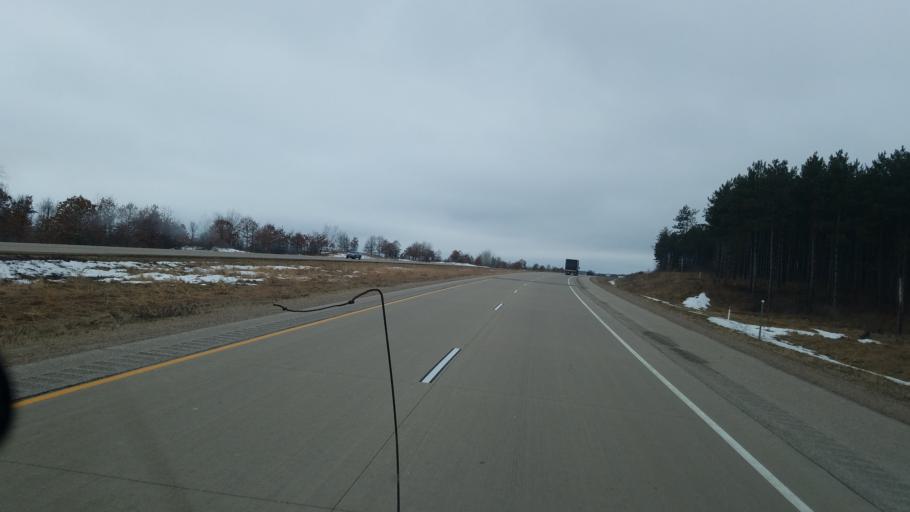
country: US
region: Wisconsin
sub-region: Portage County
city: Amherst
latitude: 44.5024
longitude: -89.4023
